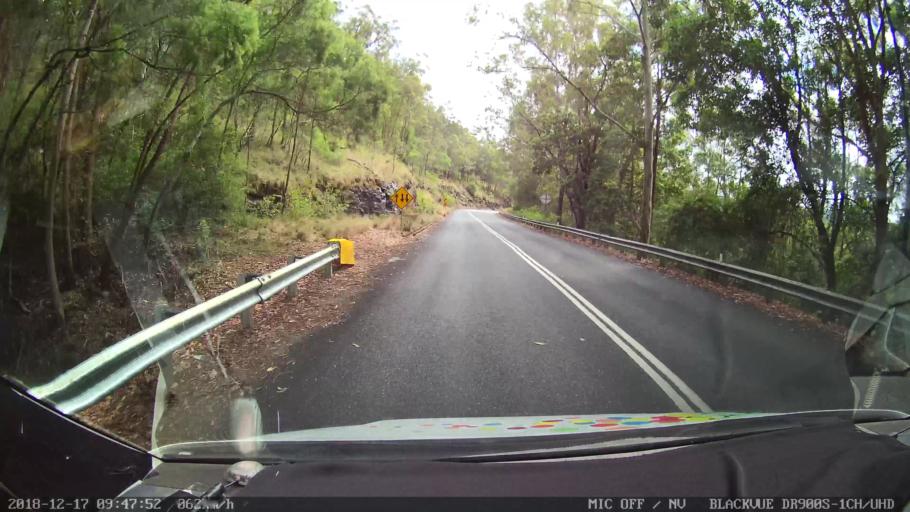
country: AU
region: New South Wales
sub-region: Tenterfield Municipality
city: Carrolls Creek
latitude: -28.9261
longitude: 152.3408
